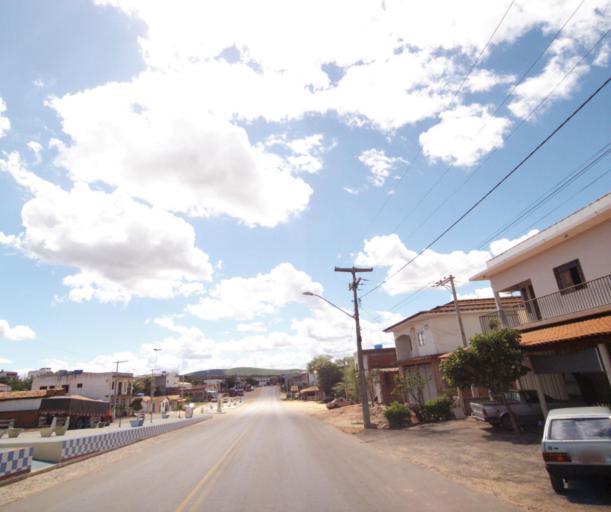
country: BR
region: Bahia
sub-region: Cacule
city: Cacule
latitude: -14.2054
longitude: -42.1155
